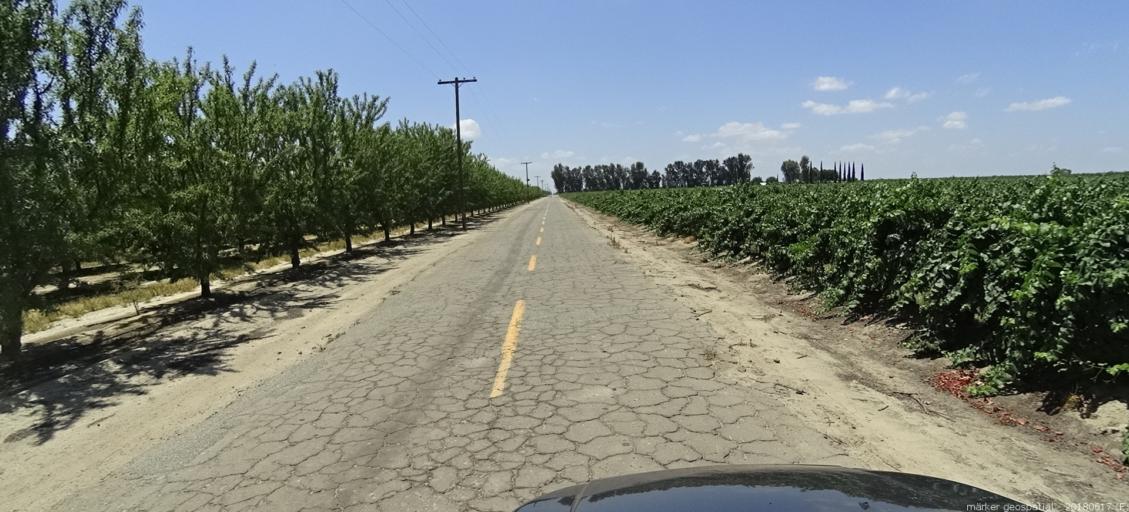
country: US
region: California
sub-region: Fresno County
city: Biola
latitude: 36.8295
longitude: -120.1560
